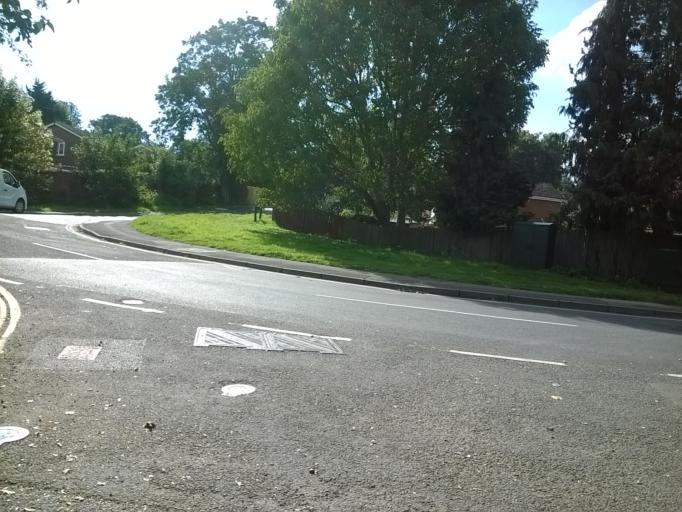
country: GB
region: England
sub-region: West Berkshire
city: Tilehurst
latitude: 51.4815
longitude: -1.0455
